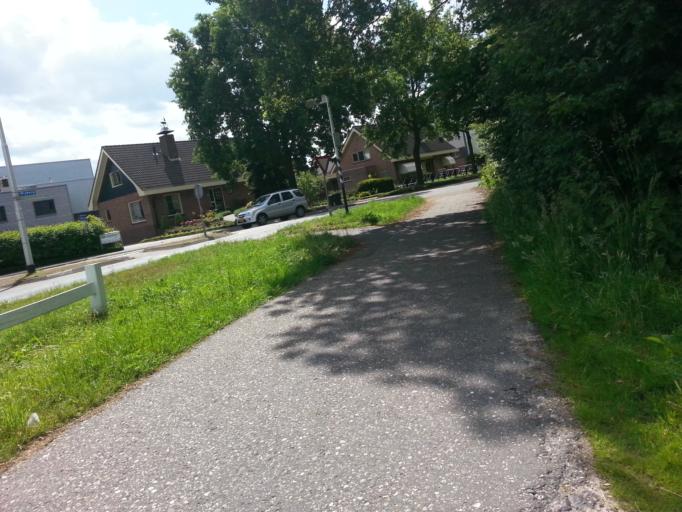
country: NL
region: Gelderland
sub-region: Gemeente Ede
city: Ederveen
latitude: 52.0754
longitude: 5.5308
